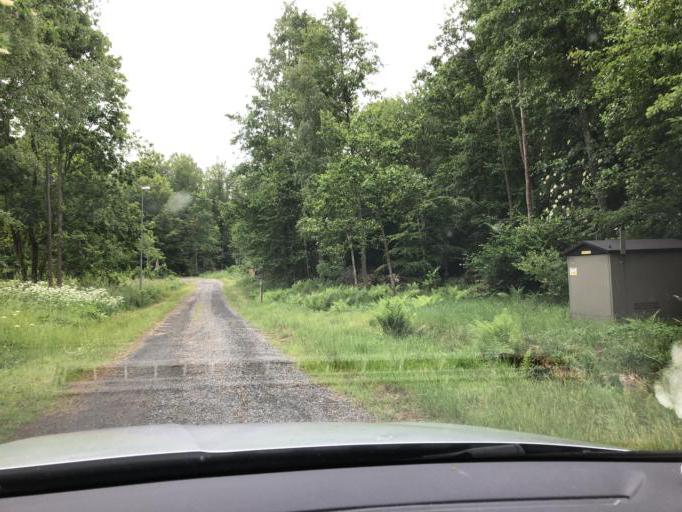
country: SE
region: Blekinge
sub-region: Solvesborgs Kommun
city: Soelvesborg
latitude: 56.1418
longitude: 14.5962
